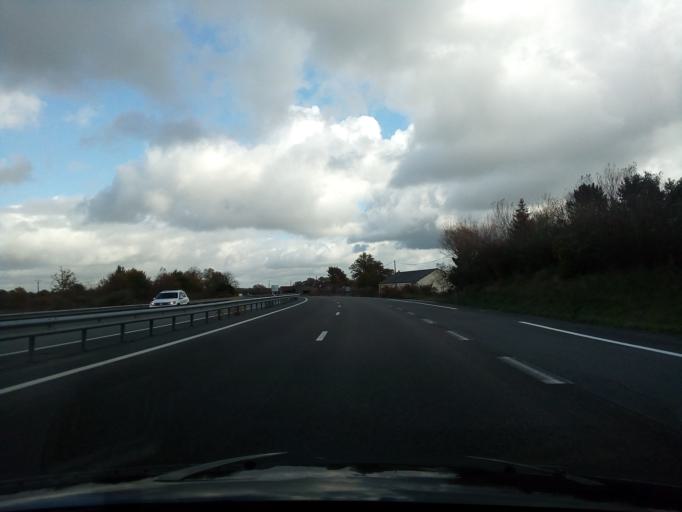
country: FR
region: Limousin
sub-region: Departement de la Creuse
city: Gouzon
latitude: 46.1986
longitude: 2.2531
